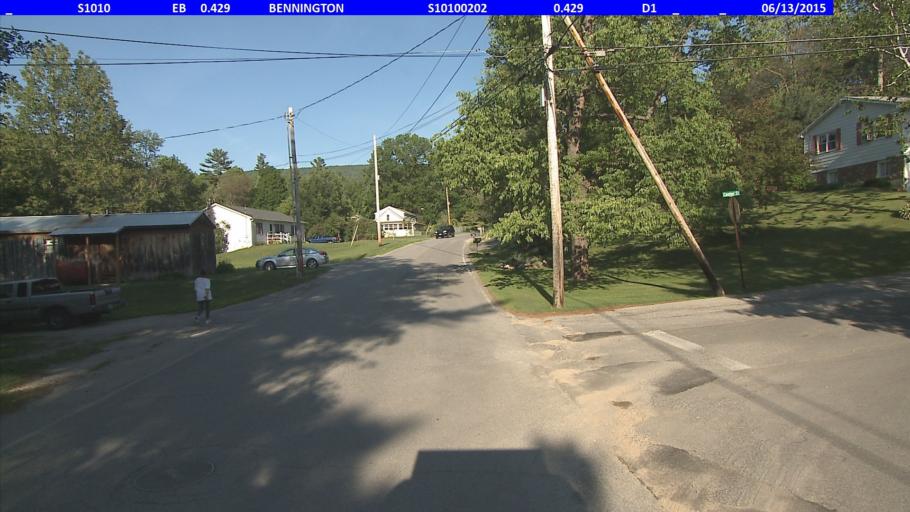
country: US
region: Vermont
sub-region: Bennington County
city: Bennington
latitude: 42.8789
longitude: -73.1673
